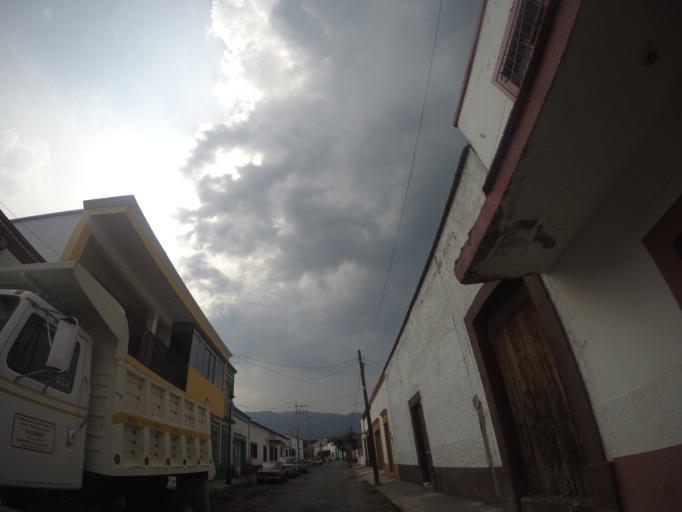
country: MX
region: Nayarit
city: Jala
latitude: 21.1038
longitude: -104.4383
